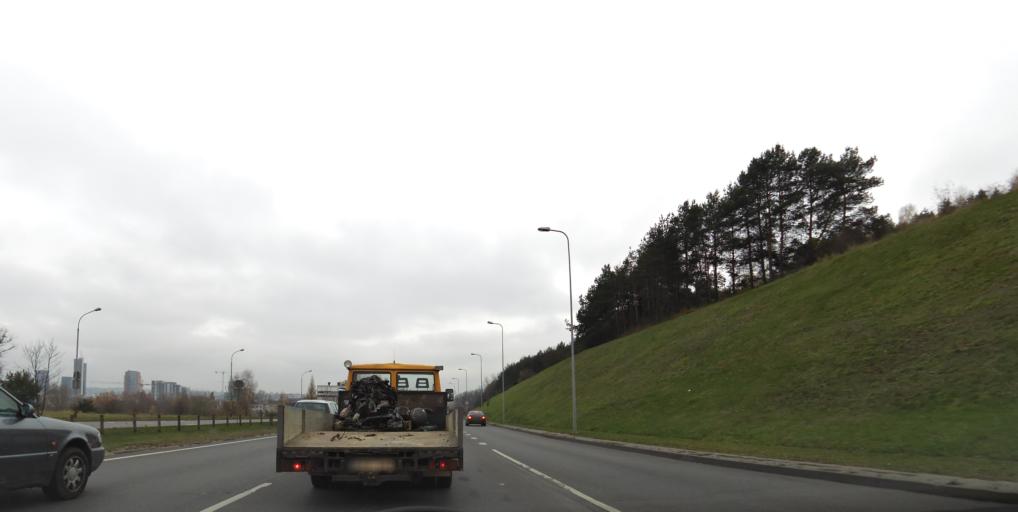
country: LT
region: Vilnius County
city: Seskine
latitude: 54.7113
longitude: 25.2697
